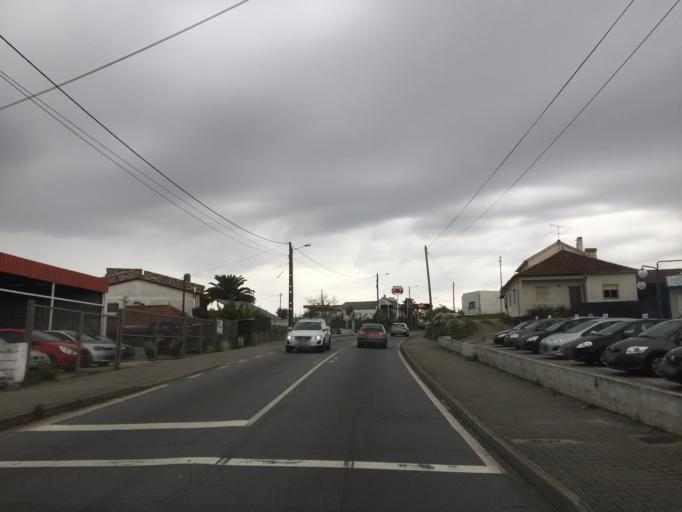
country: PT
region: Leiria
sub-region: Leiria
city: Santa Catarina da Serra
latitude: 39.6656
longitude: -8.6851
